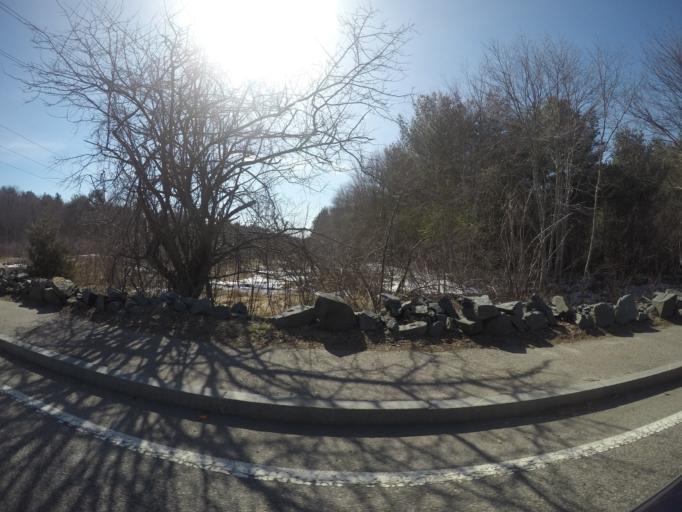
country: US
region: Massachusetts
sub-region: Bristol County
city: Easton
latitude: 42.0299
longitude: -71.1147
